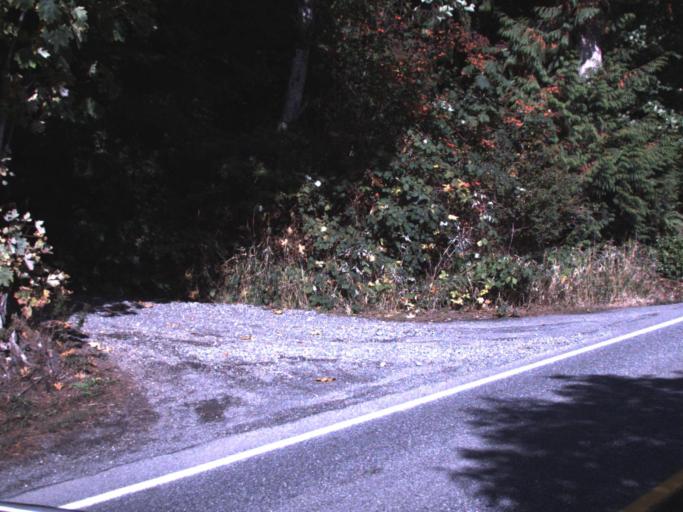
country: US
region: Washington
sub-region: Skagit County
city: Sedro-Woolley
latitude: 48.6227
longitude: -122.2215
